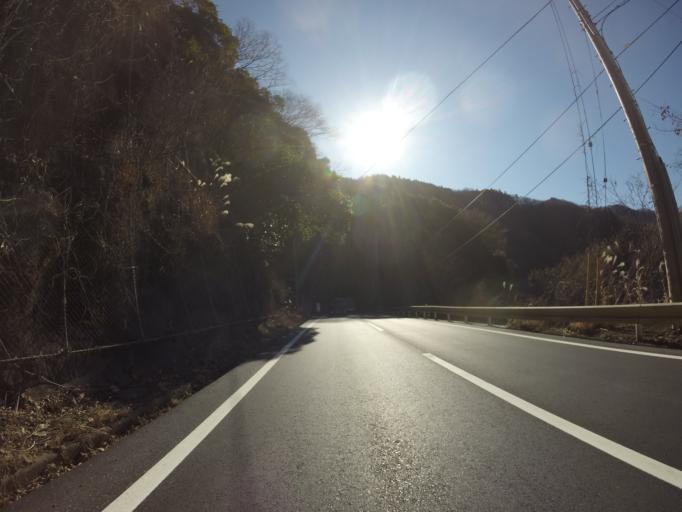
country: JP
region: Yamanashi
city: Ryuo
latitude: 35.4271
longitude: 138.4097
